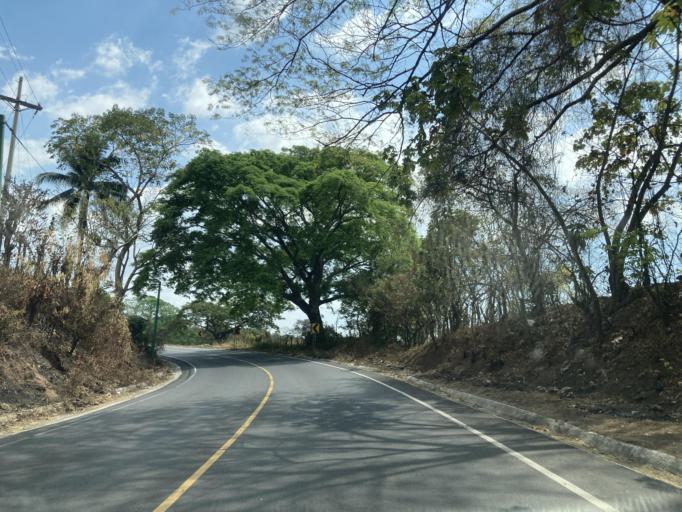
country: GT
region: Santa Rosa
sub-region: Municipio de Taxisco
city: Taxisco
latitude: 14.0626
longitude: -90.4667
